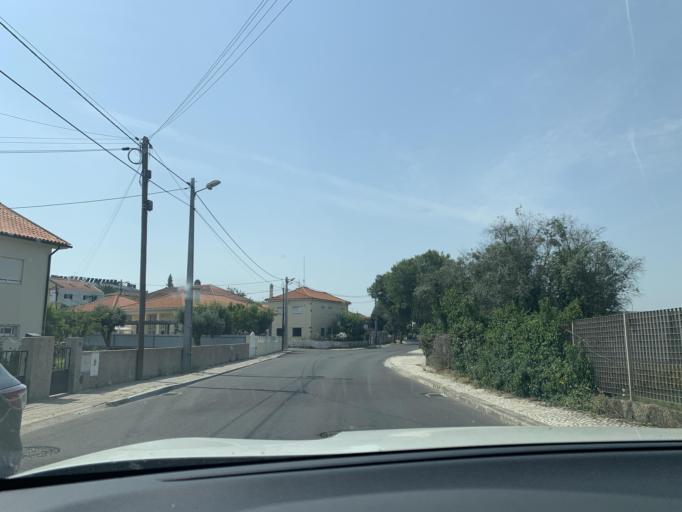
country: PT
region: Viseu
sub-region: Viseu
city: Viseu
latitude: 40.6437
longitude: -7.9181
